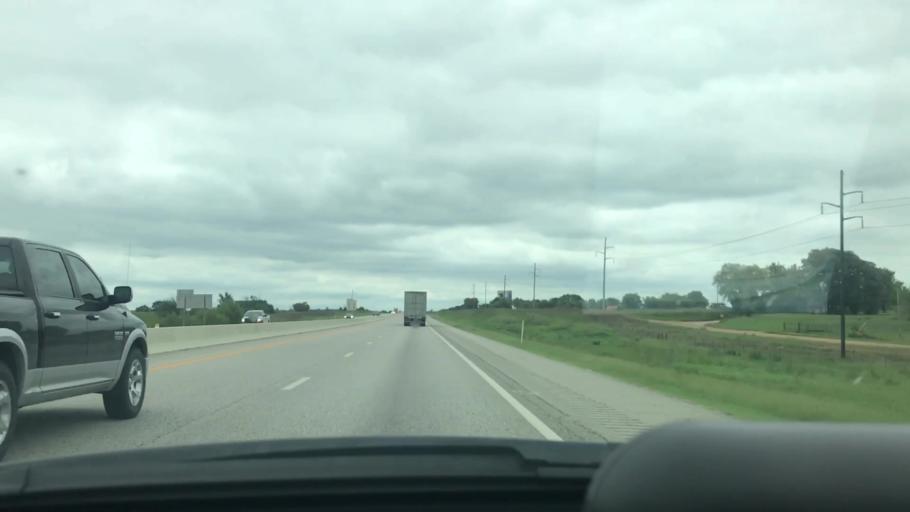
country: US
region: Oklahoma
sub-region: Craig County
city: Vinita
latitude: 36.6402
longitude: -95.1215
